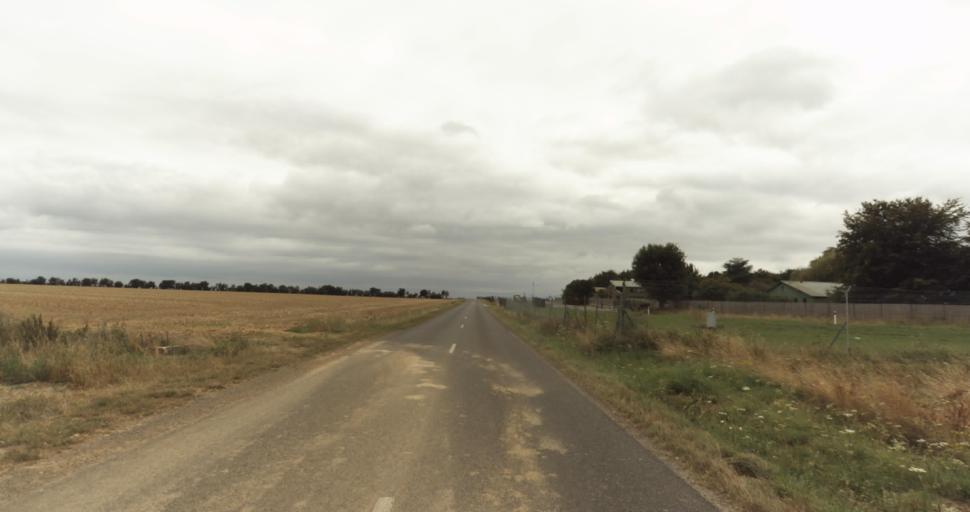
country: FR
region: Haute-Normandie
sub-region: Departement de l'Eure
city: Gravigny
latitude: 49.0468
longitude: 1.2303
